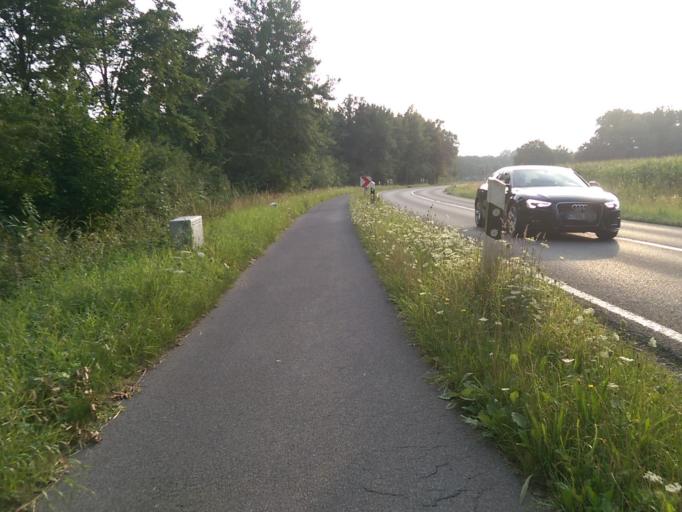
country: DE
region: North Rhine-Westphalia
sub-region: Regierungsbezirk Detmold
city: Rheda-Wiedenbruck
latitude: 51.8861
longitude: 8.2685
